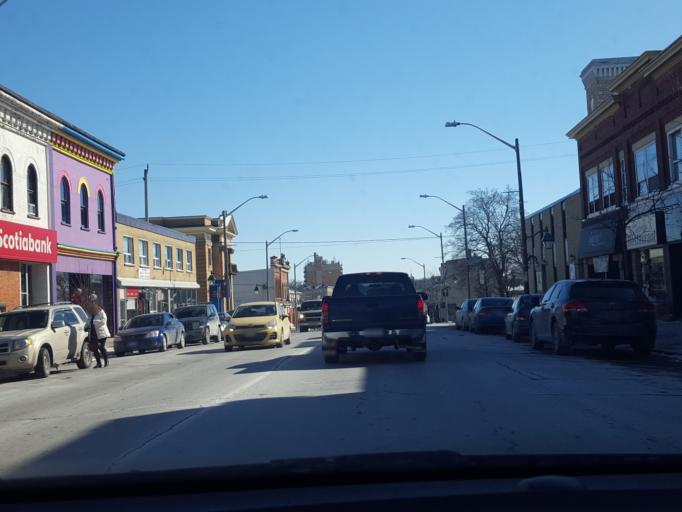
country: CA
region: Ontario
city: Cambridge
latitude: 43.3955
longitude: -80.3578
